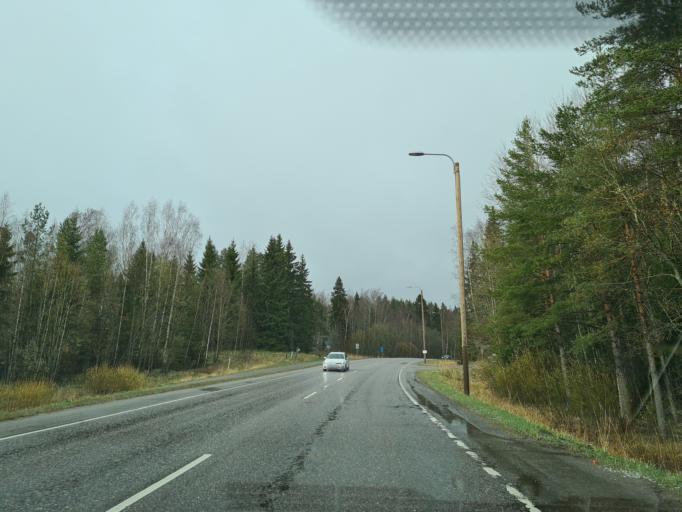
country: FI
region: Uusimaa
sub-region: Helsinki
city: Kirkkonummi
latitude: 60.0983
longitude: 24.4165
